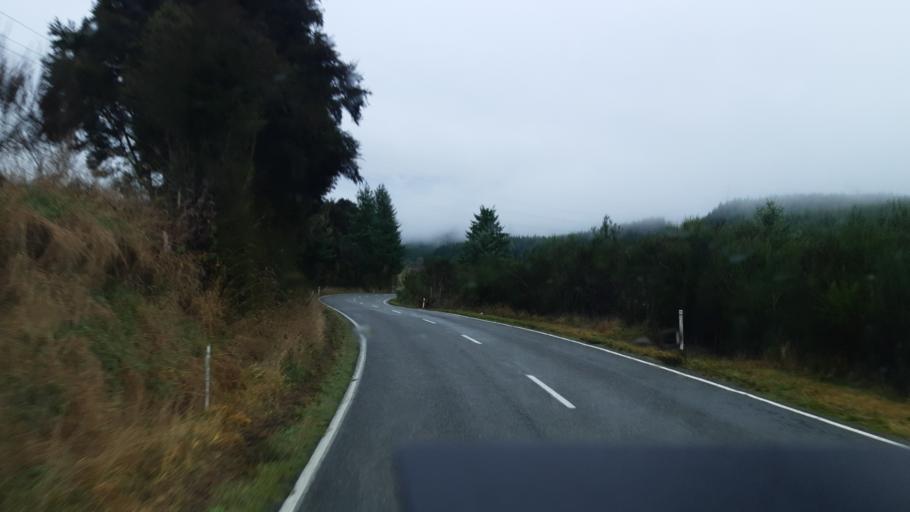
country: NZ
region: Tasman
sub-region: Tasman District
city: Wakefield
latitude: -41.6720
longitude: 172.8760
